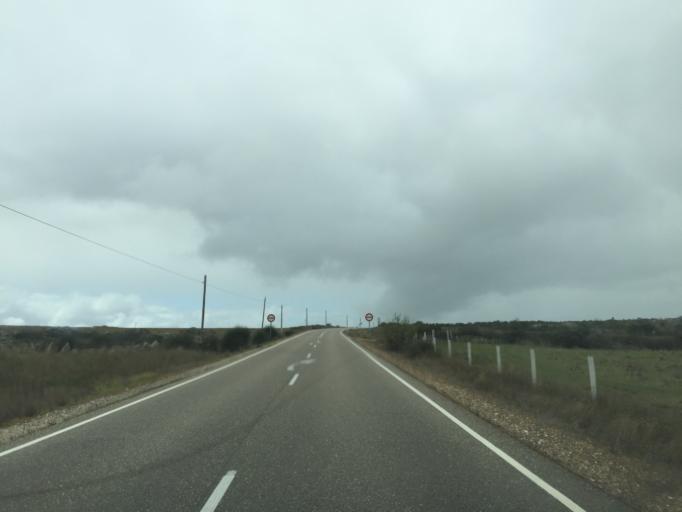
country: ES
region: Castille and Leon
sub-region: Provincia de Zamora
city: Villalcampo
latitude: 41.5252
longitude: -6.0296
